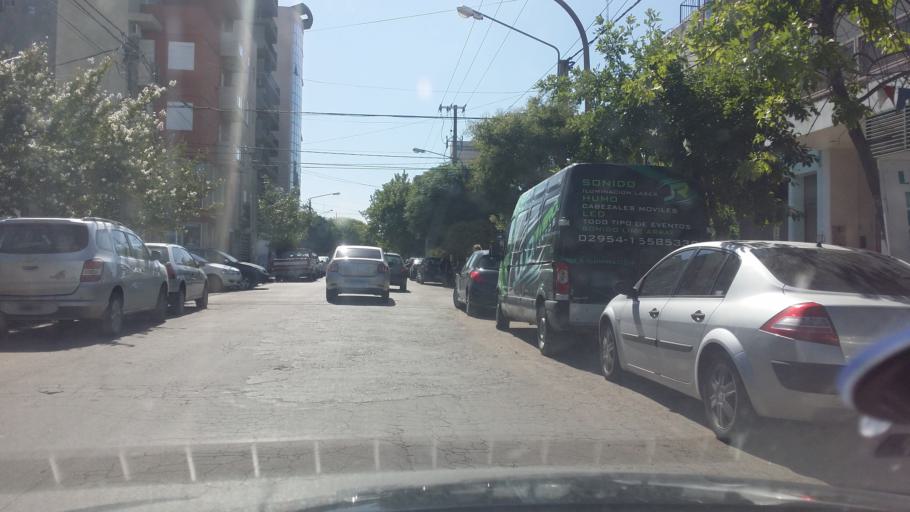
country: AR
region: La Pampa
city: Santa Rosa
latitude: -36.6220
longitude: -64.2864
